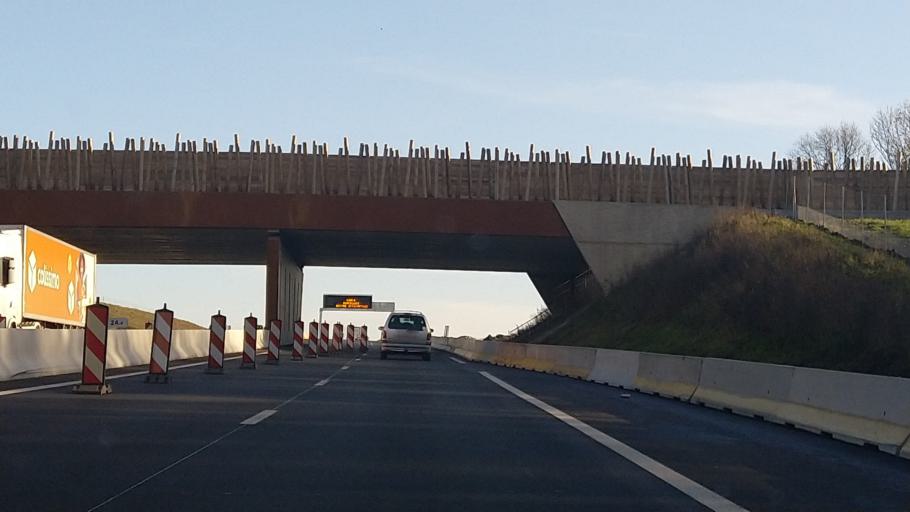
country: FR
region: Ile-de-France
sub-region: Departement du Val-d'Oise
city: Maffliers
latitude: 49.0909
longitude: 2.3066
